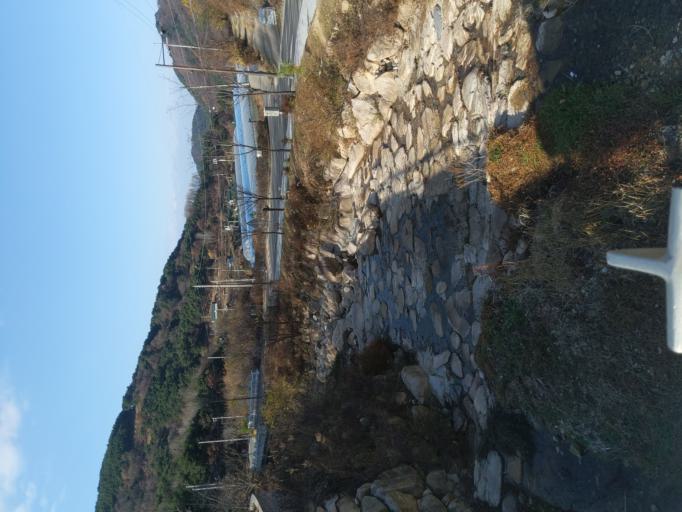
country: KR
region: Daegu
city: Hwawon
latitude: 35.7746
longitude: 128.5351
